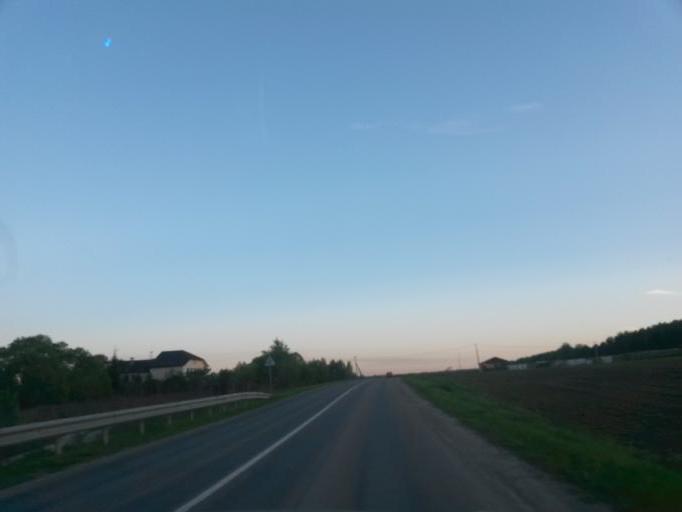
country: RU
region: Moskovskaya
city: Lyubuchany
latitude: 55.2926
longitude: 37.6290
